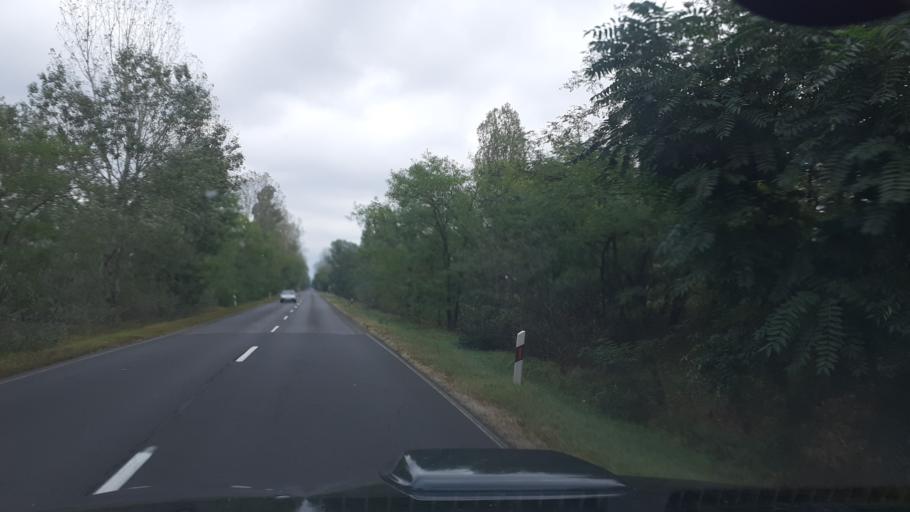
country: HU
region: Bacs-Kiskun
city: Agasegyhaza
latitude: 46.8773
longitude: 19.4847
